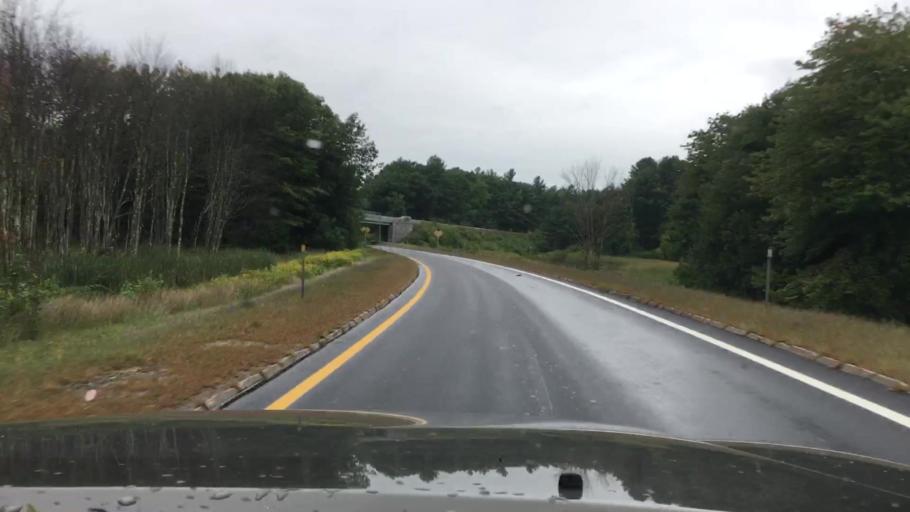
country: US
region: New Hampshire
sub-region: Merrimack County
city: Hopkinton
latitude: 43.1817
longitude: -71.6838
